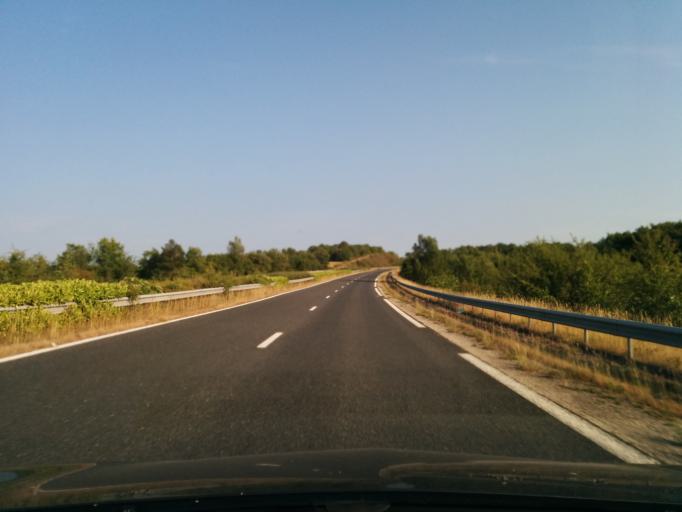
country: FR
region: Midi-Pyrenees
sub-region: Departement du Lot
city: Souillac
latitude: 44.8248
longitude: 1.4747
